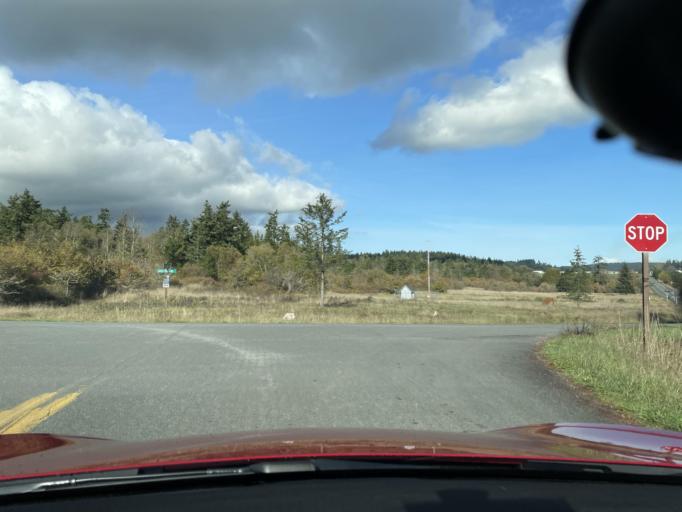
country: US
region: Washington
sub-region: San Juan County
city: Friday Harbor
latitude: 48.5110
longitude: -123.0232
